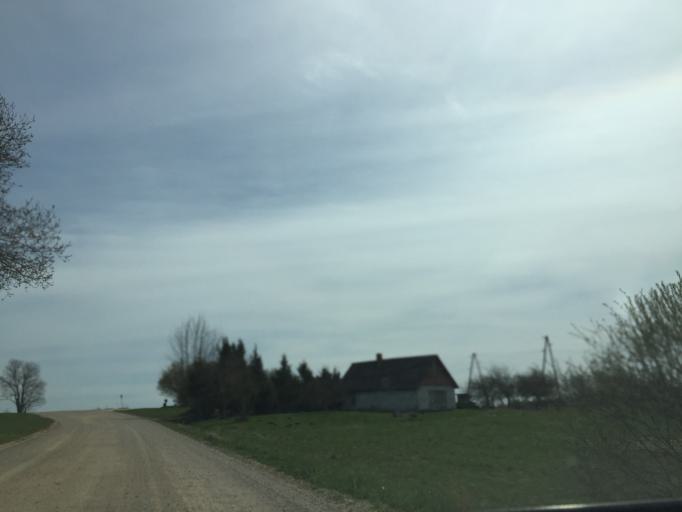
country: LV
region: Ludzas Rajons
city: Ludza
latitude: 56.5830
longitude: 27.5400
